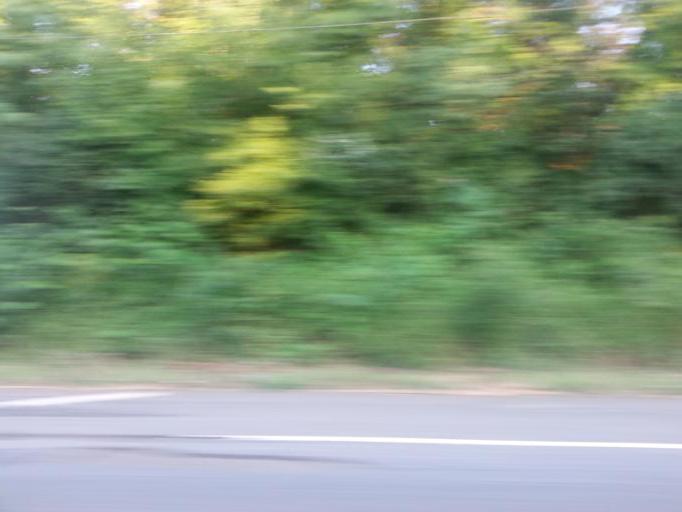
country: US
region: Tennessee
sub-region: Blount County
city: Eagleton Village
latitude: 35.8788
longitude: -83.9583
